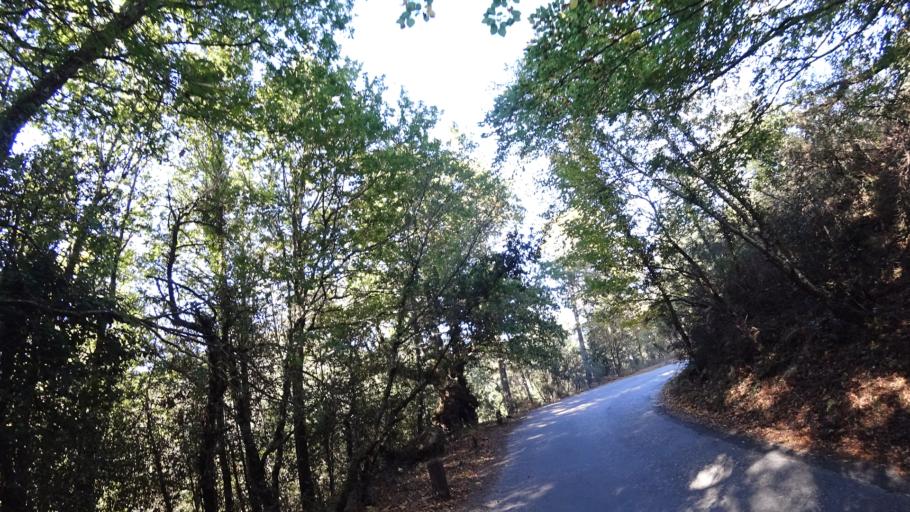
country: ES
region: Galicia
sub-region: Provincia de Ourense
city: Lobios
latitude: 41.7917
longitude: -8.1358
